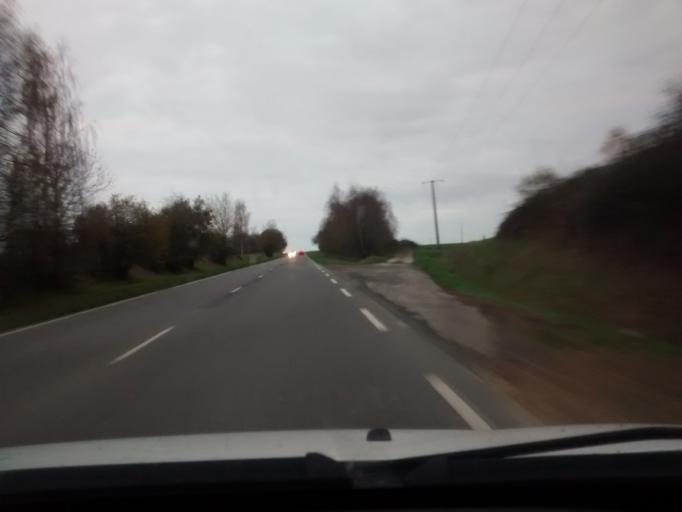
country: FR
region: Brittany
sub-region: Departement d'Ille-et-Vilaine
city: Cesson-Sevigne
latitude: 48.1365
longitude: -1.5900
